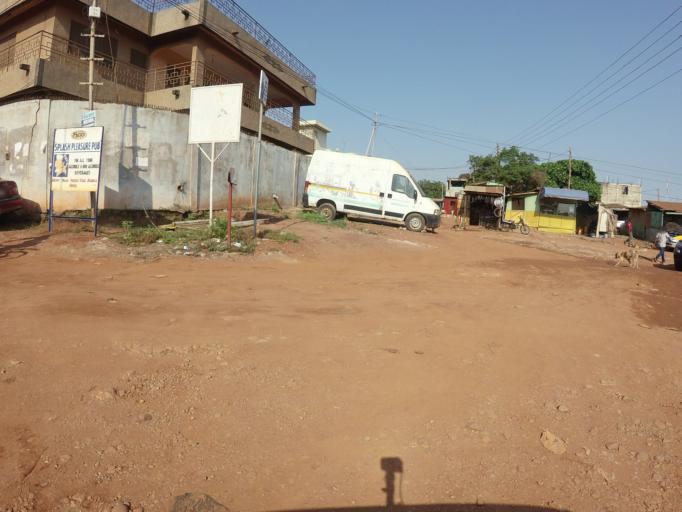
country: GH
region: Greater Accra
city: Dome
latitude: 5.6094
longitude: -0.2431
